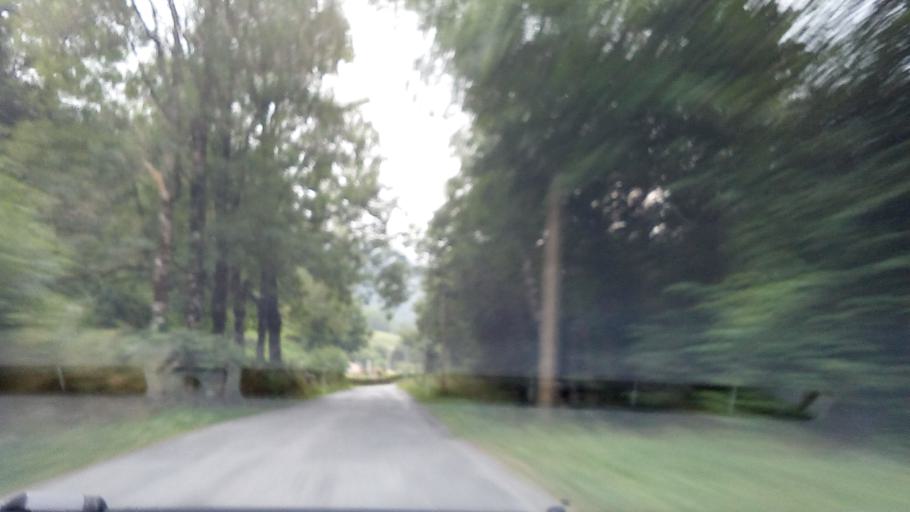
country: FR
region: Midi-Pyrenees
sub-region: Departement des Hautes-Pyrenees
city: Cauterets
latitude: 42.9316
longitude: -0.1797
